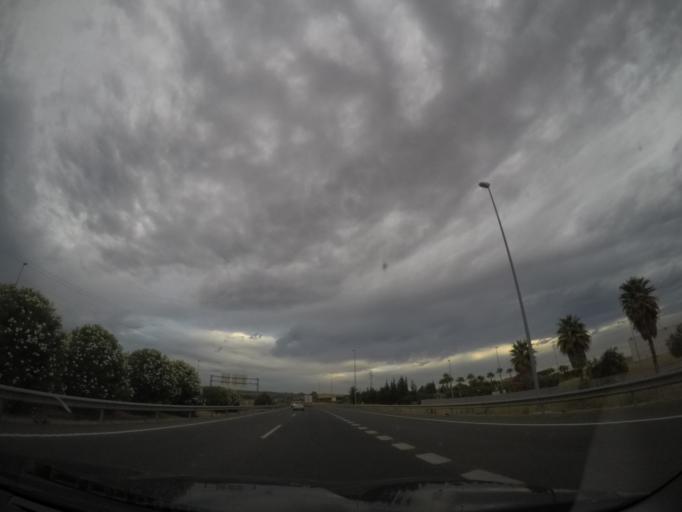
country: ES
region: Andalusia
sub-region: Provincia de Sevilla
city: Carrion de los Cespedes
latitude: 37.3590
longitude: -6.3293
